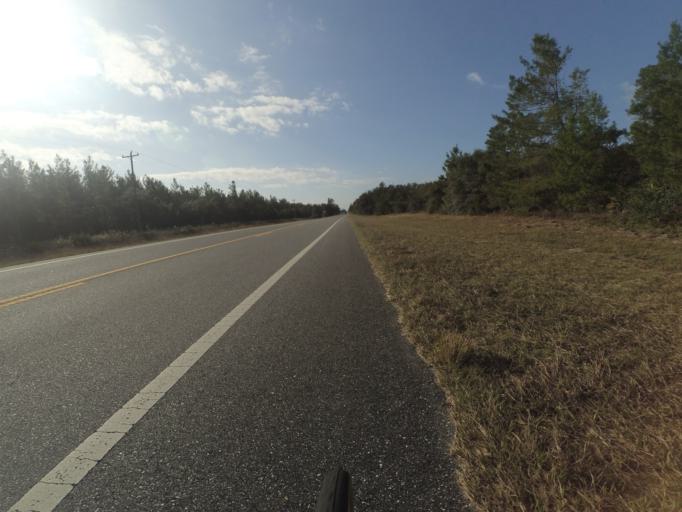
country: US
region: Florida
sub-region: Lake County
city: Astor
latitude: 29.1066
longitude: -81.6180
